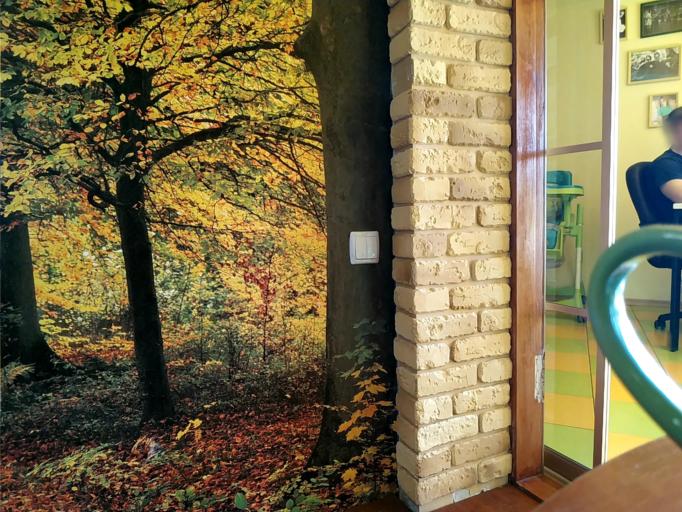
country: RU
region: Moskovskaya
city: Krasnoarmeysk
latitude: 56.0729
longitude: 38.2597
